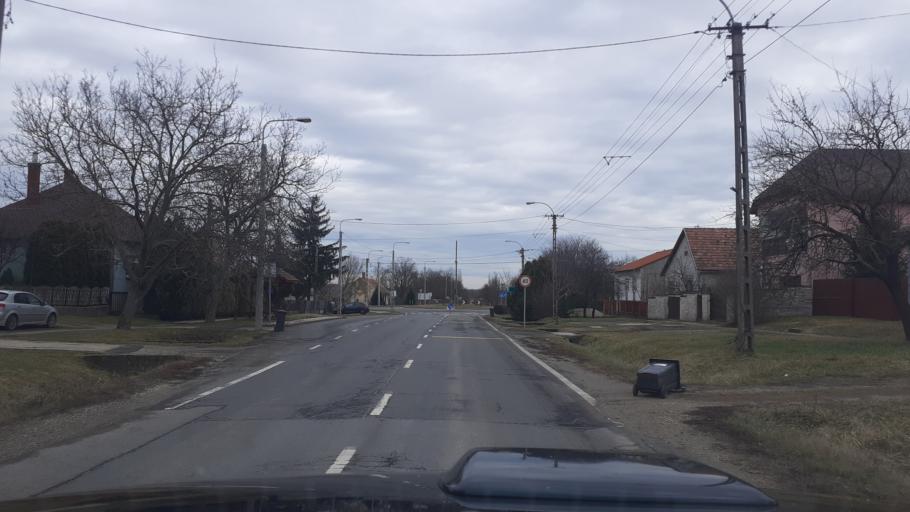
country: HU
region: Fejer
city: Mezofalva
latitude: 46.9297
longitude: 18.7850
